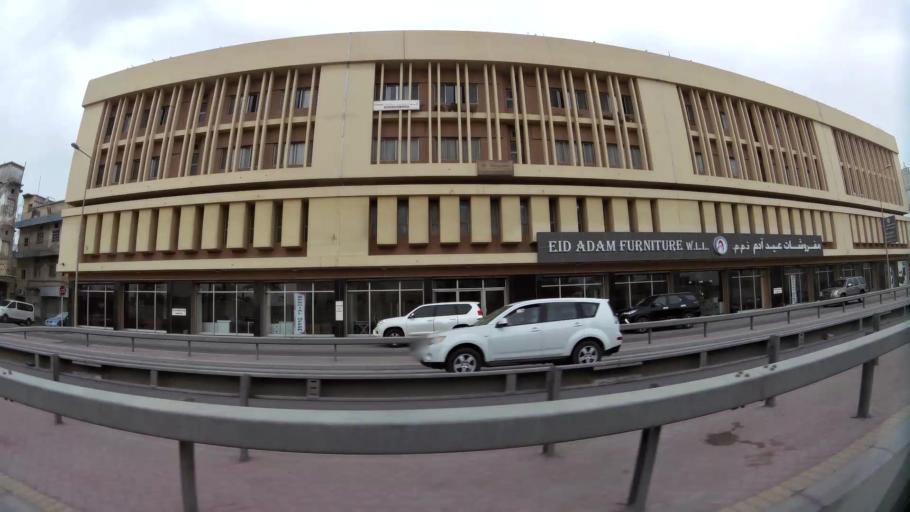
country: BH
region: Manama
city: Jidd Hafs
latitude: 26.2079
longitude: 50.5481
